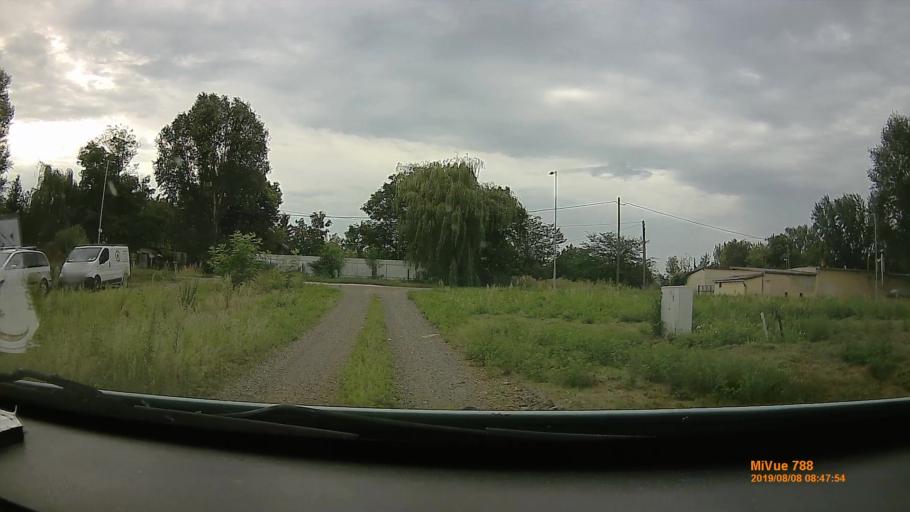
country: HU
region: Hajdu-Bihar
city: Debrecen
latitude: 47.5971
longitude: 21.6383
